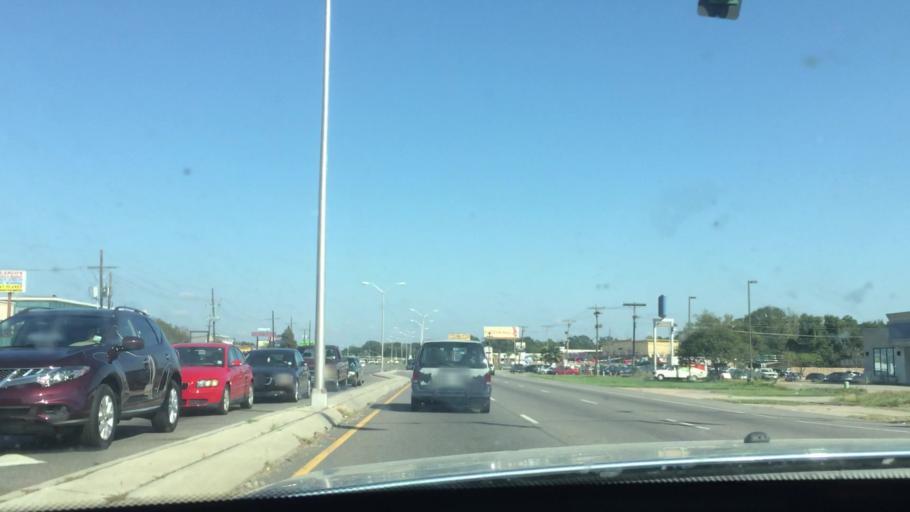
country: US
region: Louisiana
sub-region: East Baton Rouge Parish
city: Westminster
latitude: 30.4520
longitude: -91.1038
